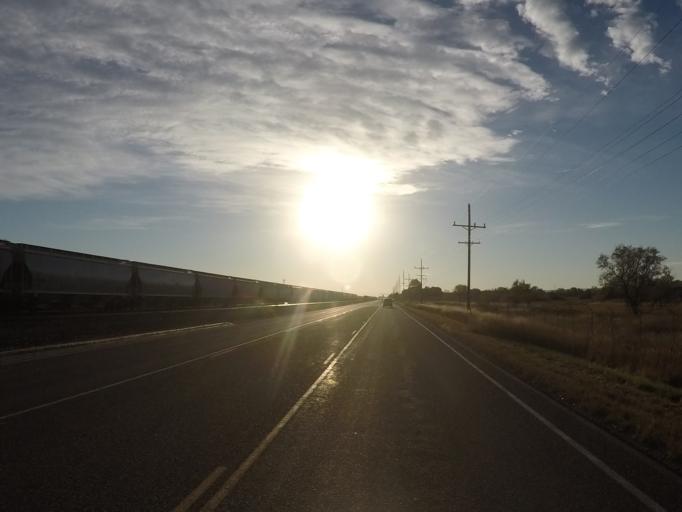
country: US
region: Montana
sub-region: Yellowstone County
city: Laurel
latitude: 45.6783
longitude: -108.7339
